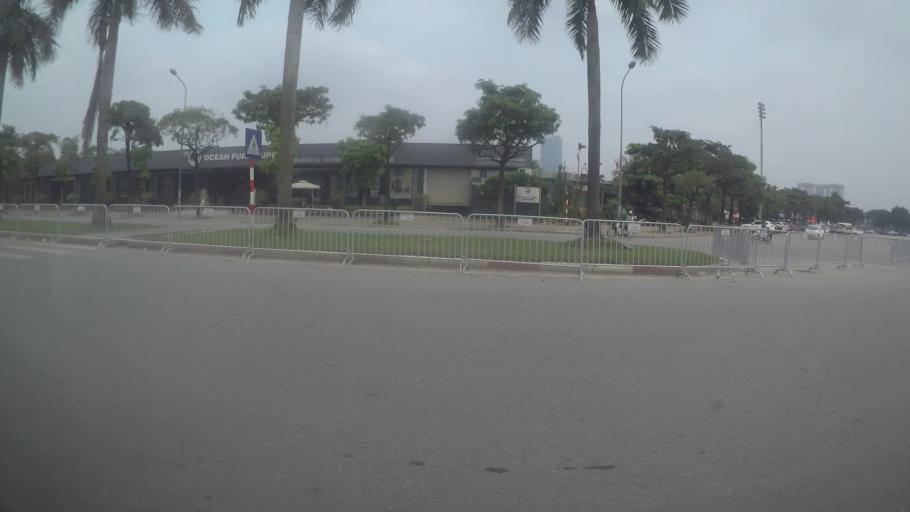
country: VN
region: Ha Noi
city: Cau Dien
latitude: 21.0222
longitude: 105.7669
